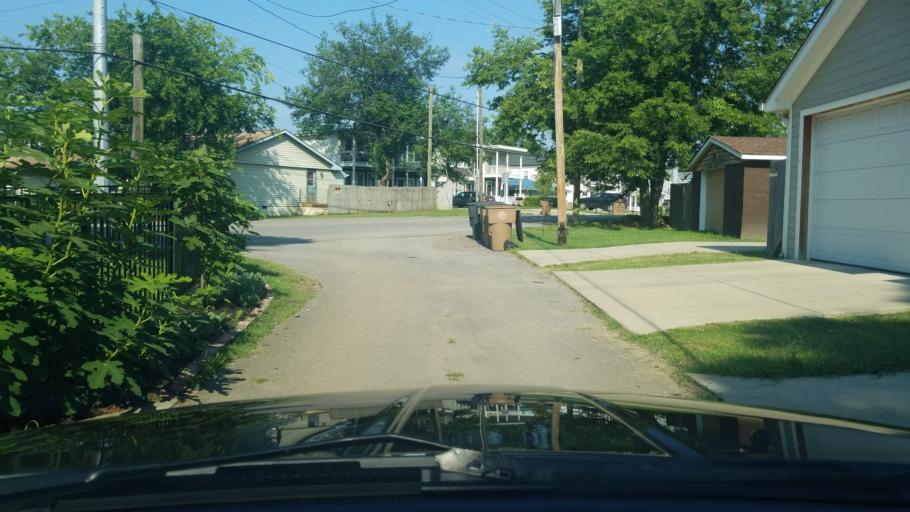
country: US
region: Tennessee
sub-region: Davidson County
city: Belle Meade
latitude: 36.1602
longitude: -86.8569
